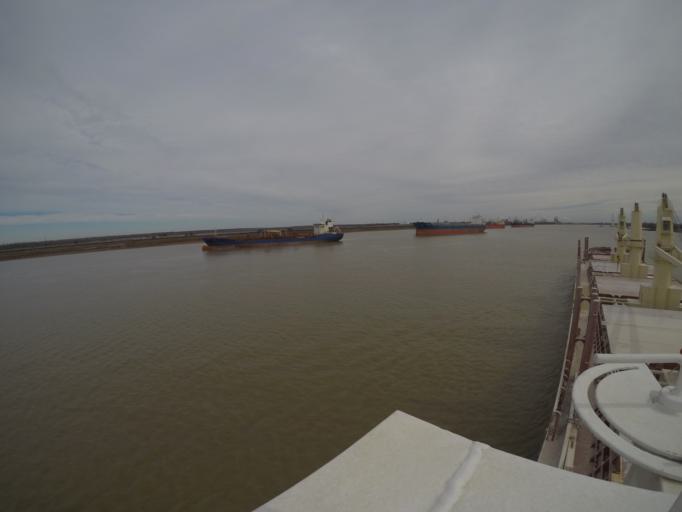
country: US
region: Louisiana
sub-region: Saint Charles Parish
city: Montz
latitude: 29.9950
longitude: -90.4473
